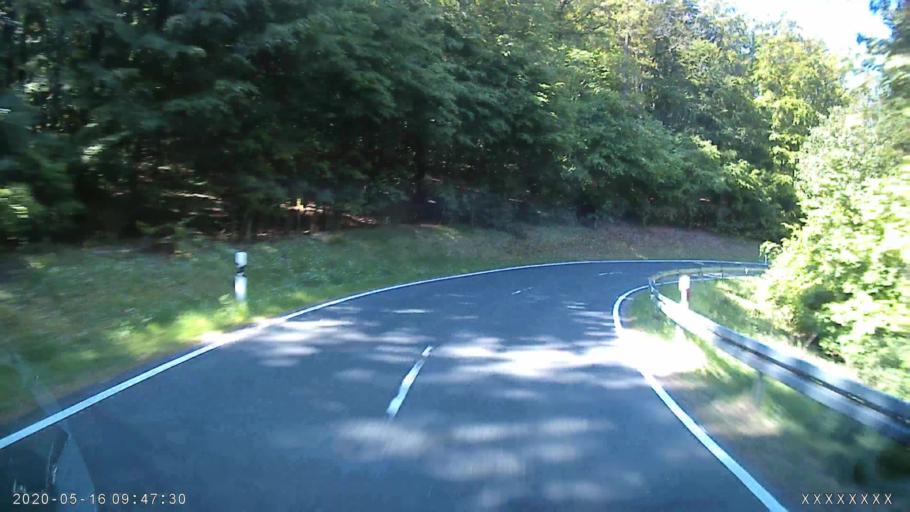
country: DE
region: Hesse
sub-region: Regierungsbezirk Giessen
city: Haiger
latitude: 50.7337
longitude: 8.2203
